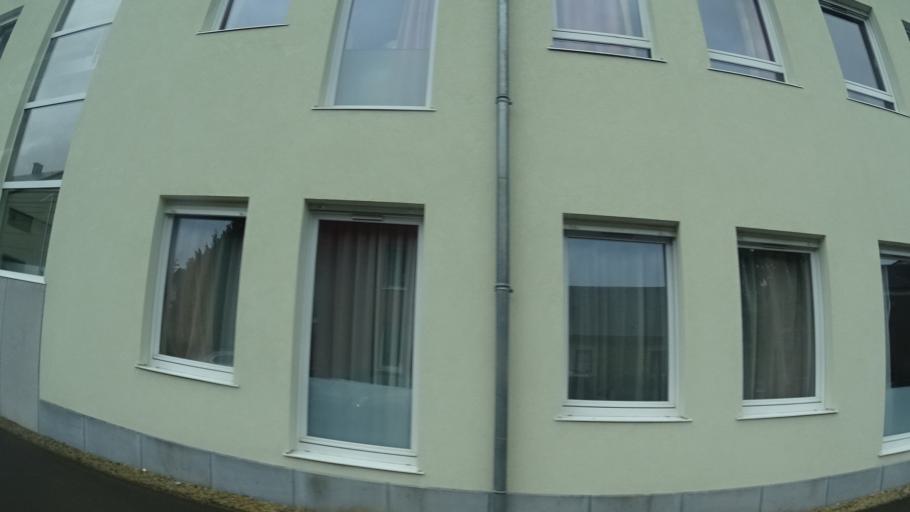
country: BE
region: Wallonia
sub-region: Province du Luxembourg
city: Messancy
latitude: 49.5923
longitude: 5.8197
